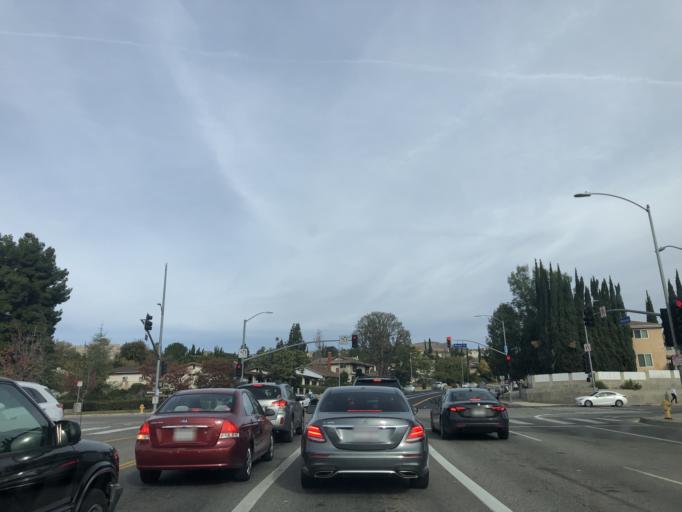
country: US
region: California
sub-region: Los Angeles County
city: Northridge
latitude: 34.2756
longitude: -118.5364
